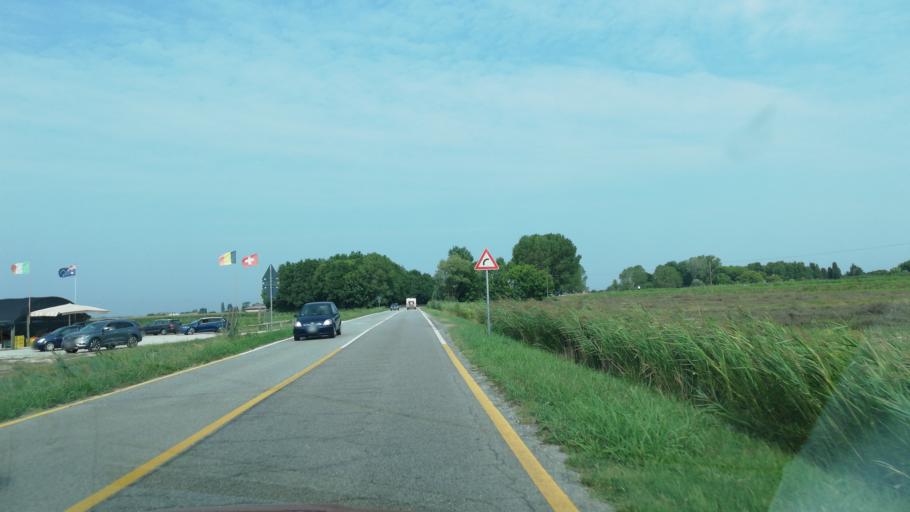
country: IT
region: Veneto
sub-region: Provincia di Venezia
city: La Salute di Livenza
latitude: 45.5942
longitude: 12.8096
